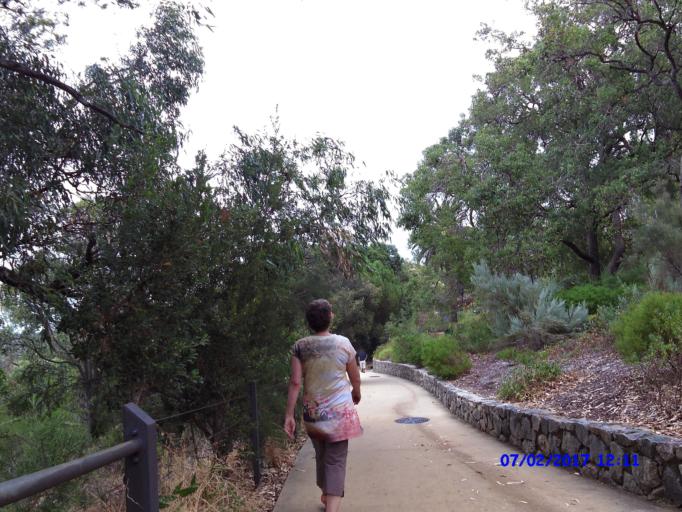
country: AU
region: Western Australia
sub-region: City of Perth
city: West Perth
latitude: -31.9615
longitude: 115.8433
